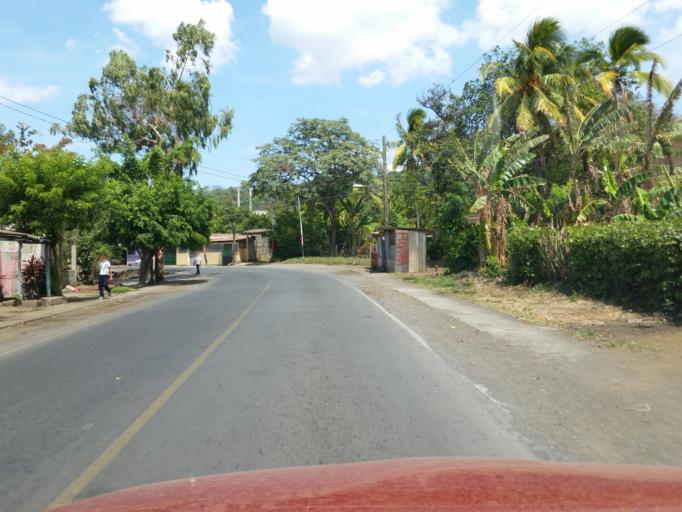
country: NI
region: Masaya
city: La Concepcion
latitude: 11.9529
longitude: -86.1894
